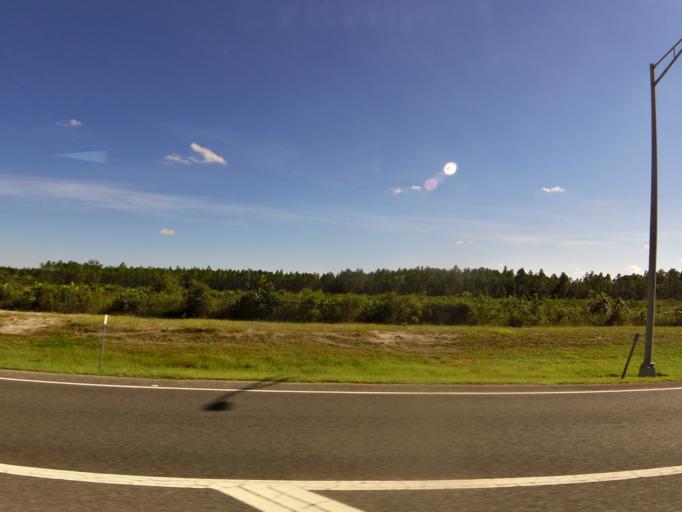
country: US
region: Florida
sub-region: Saint Johns County
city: Palm Valley
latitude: 30.1129
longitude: -81.4410
